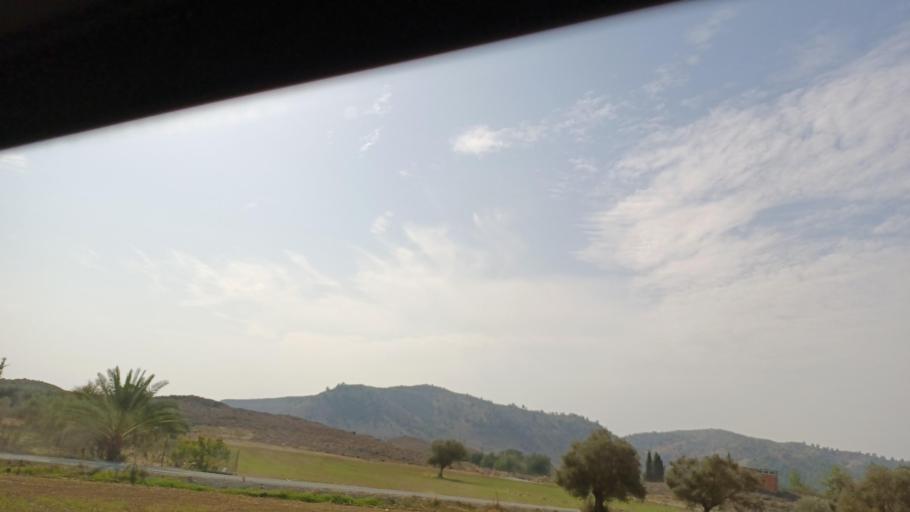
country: CY
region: Larnaka
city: Mosfiloti
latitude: 34.9703
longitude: 33.4464
